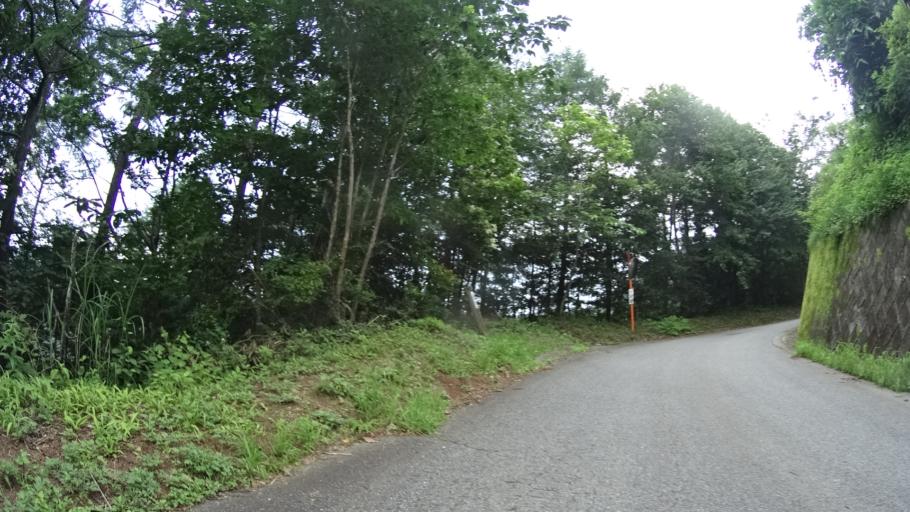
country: JP
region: Nagano
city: Saku
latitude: 36.0925
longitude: 138.6807
